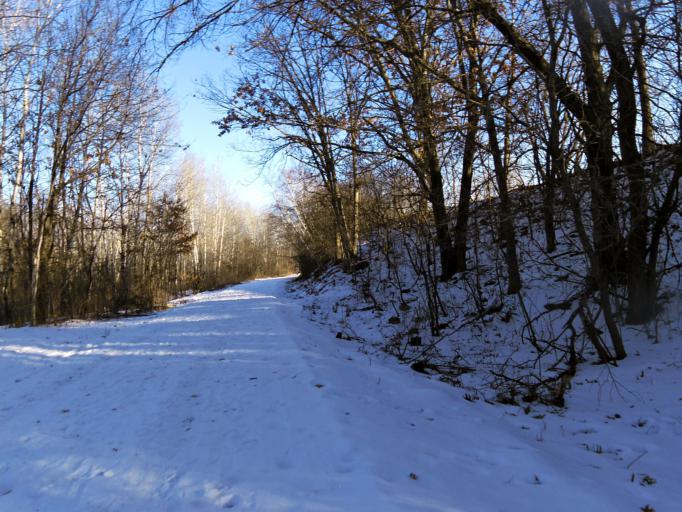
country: US
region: Minnesota
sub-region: Washington County
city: Grant
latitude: 45.0789
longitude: -92.8820
